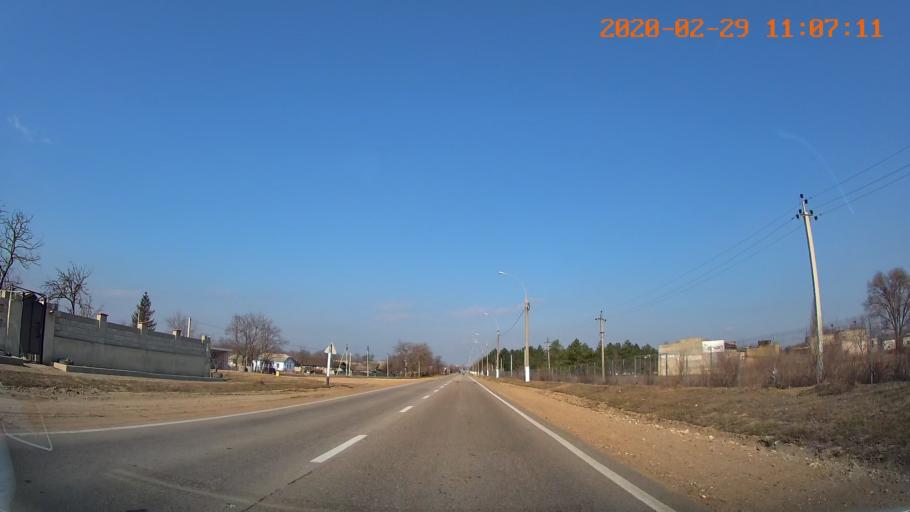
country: MD
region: Criuleni
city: Criuleni
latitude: 47.2229
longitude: 29.1838
